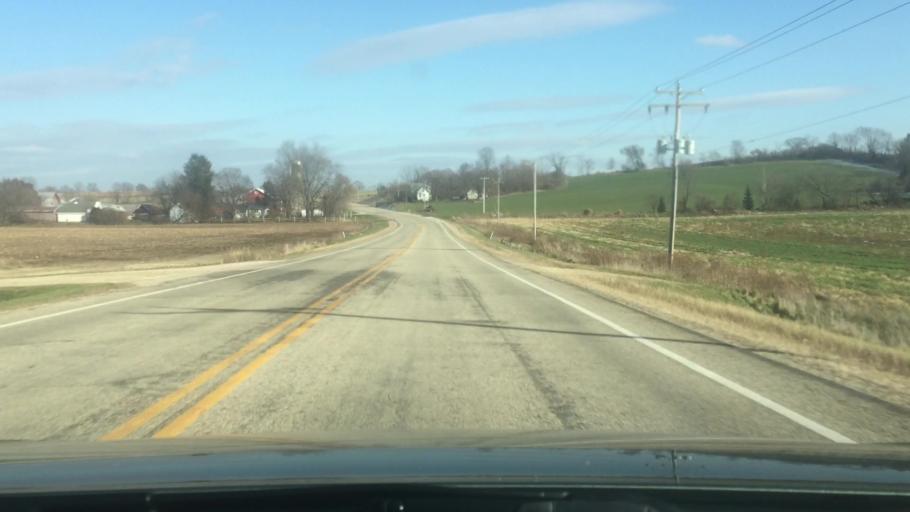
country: US
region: Wisconsin
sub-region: Jefferson County
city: Palmyra
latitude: 42.9325
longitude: -88.6533
